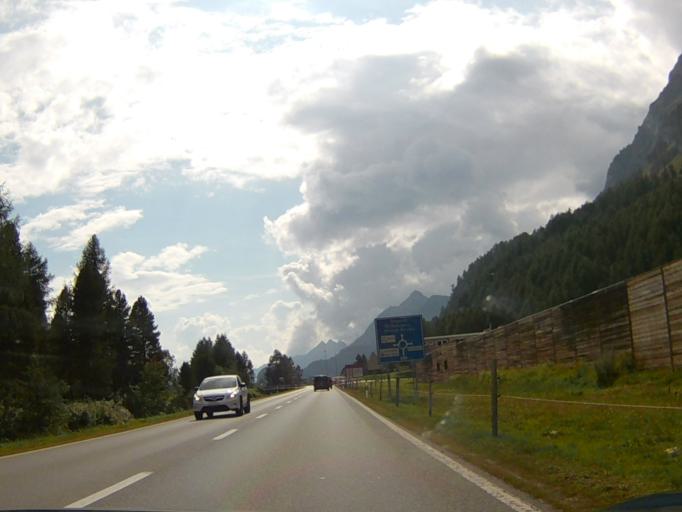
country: CH
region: Grisons
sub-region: Maloja District
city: Silvaplana
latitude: 46.4400
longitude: 9.7686
